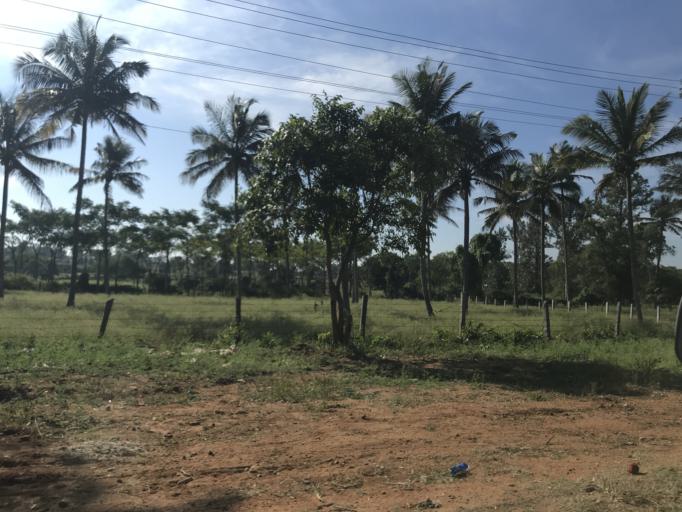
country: IN
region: Karnataka
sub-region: Mysore
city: Mysore
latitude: 12.2140
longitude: 76.5642
